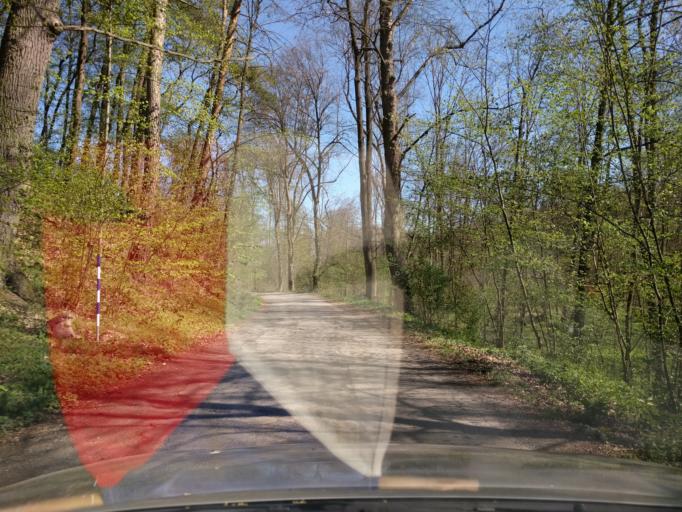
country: CZ
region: Central Bohemia
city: Cesky Brod
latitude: 50.0423
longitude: 14.8398
